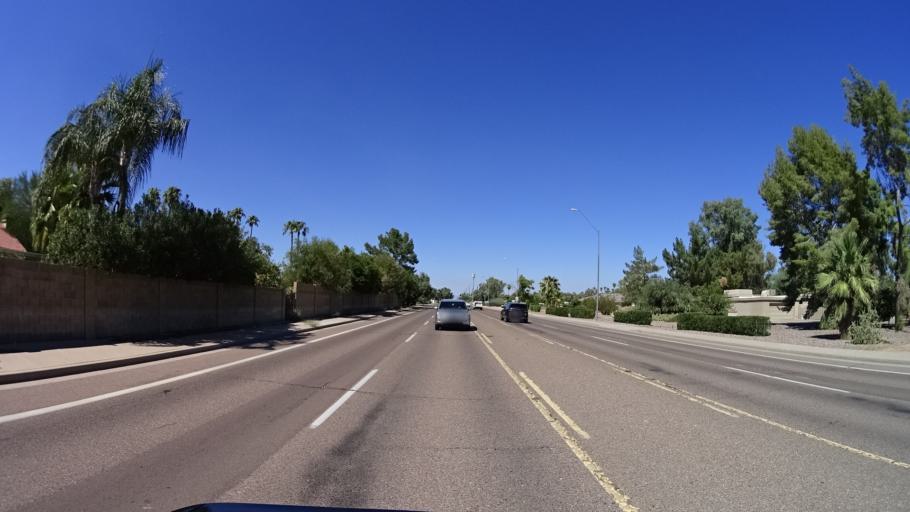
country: US
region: Arizona
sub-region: Maricopa County
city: Paradise Valley
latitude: 33.5950
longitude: -111.9606
